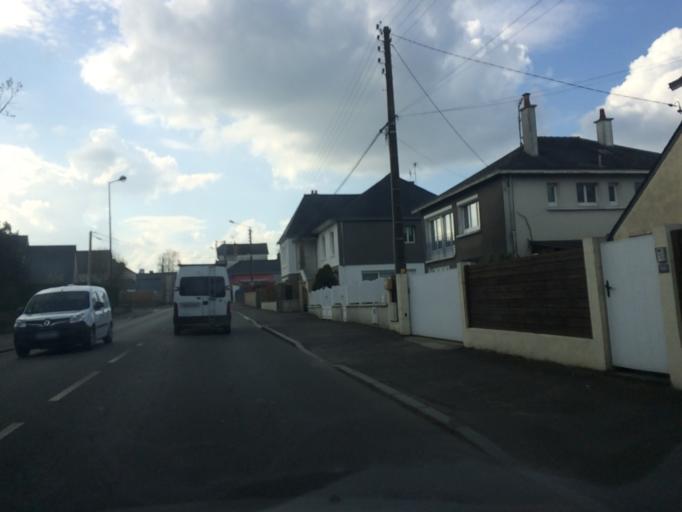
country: FR
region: Pays de la Loire
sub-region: Departement de la Loire-Atlantique
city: Blain
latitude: 47.4752
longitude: -1.7577
